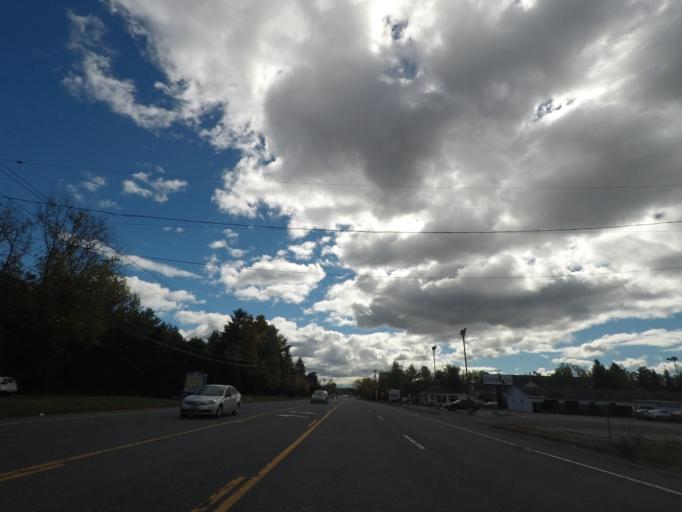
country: US
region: New York
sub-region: Saratoga County
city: Waterford
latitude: 42.8439
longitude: -73.7483
